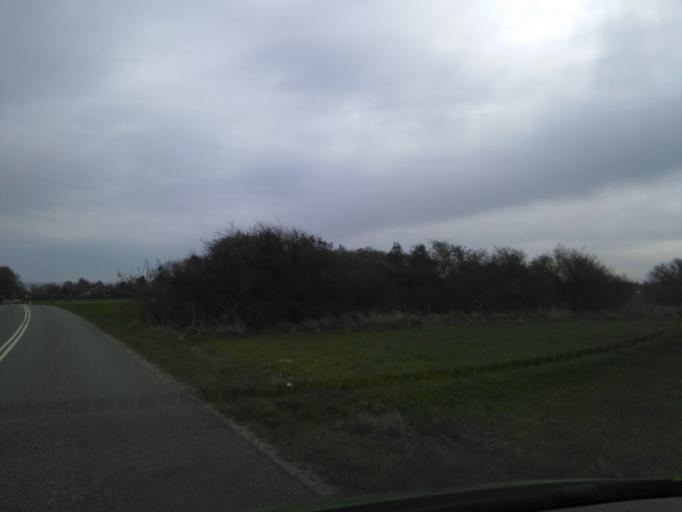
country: DK
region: Central Jutland
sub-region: Arhus Kommune
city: Beder
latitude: 56.0297
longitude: 10.2553
